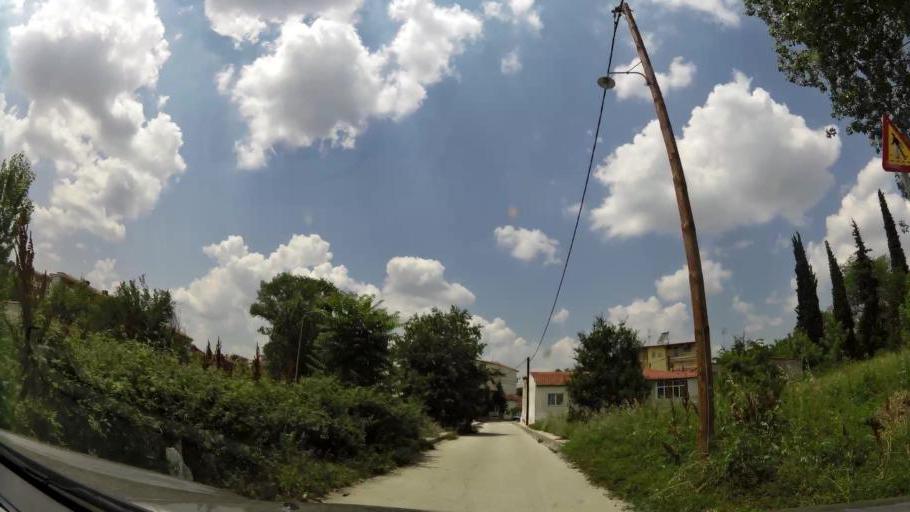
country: GR
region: West Macedonia
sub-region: Nomos Kozanis
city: Kozani
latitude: 40.2936
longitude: 21.7900
